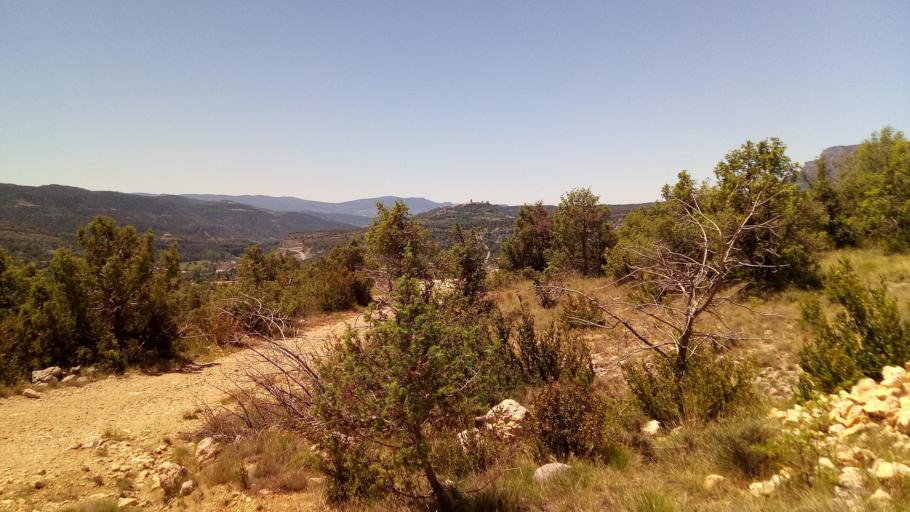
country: ES
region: Aragon
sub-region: Provincia de Huesca
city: Castigaleu
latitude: 42.3198
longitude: 0.5456
